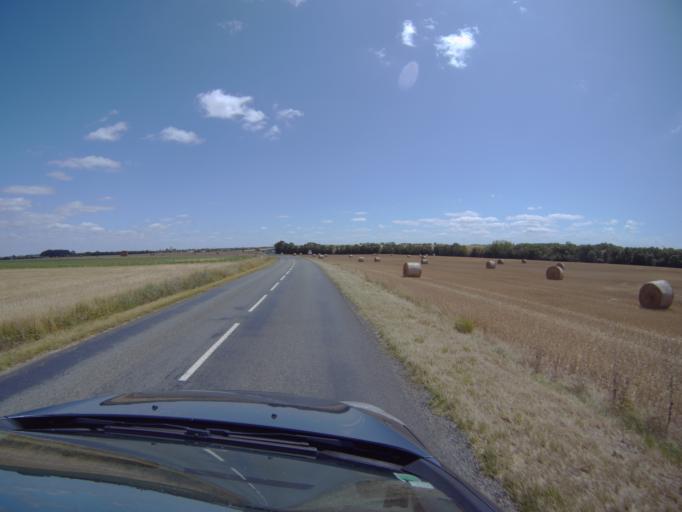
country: FR
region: Poitou-Charentes
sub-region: Departement de la Charente-Maritime
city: Courcon
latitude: 46.2522
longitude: -0.8345
